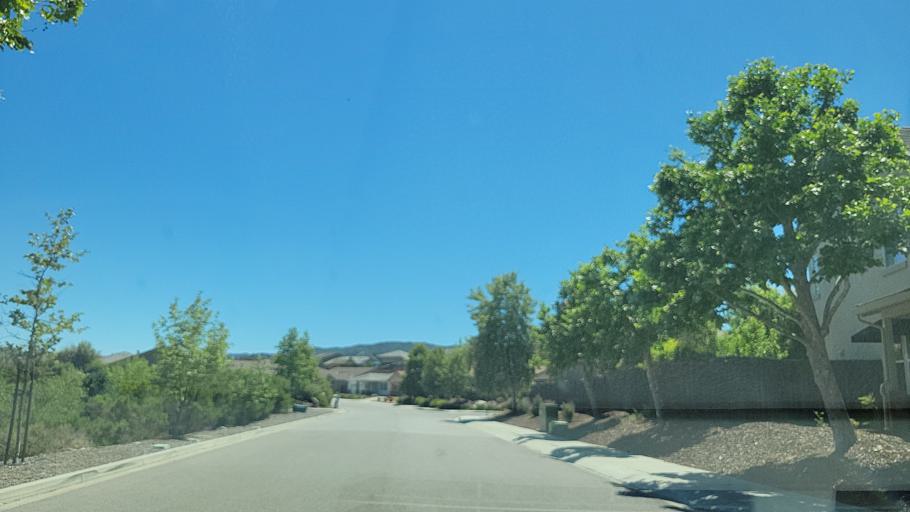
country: US
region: California
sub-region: San Luis Obispo County
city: Atascadero
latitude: 35.4543
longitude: -120.6265
